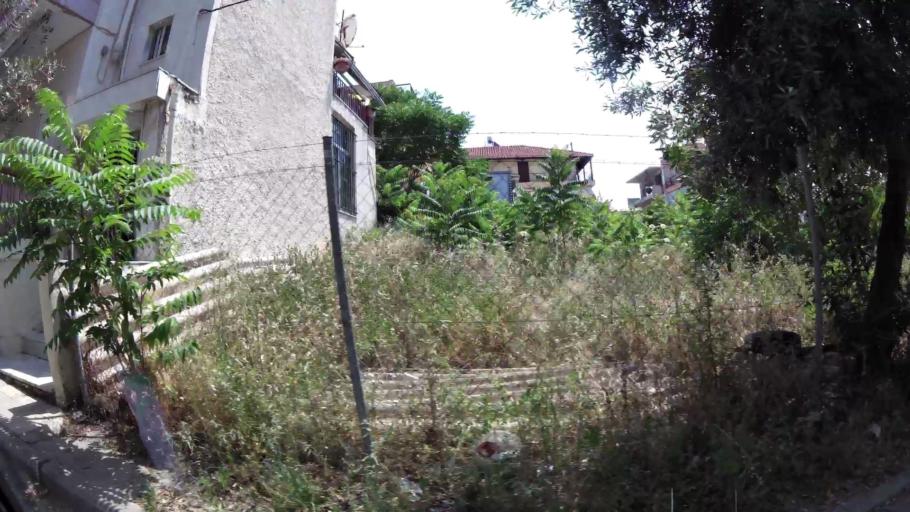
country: GR
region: Central Macedonia
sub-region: Nomos Thessalonikis
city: Evosmos
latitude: 40.6751
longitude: 22.8948
